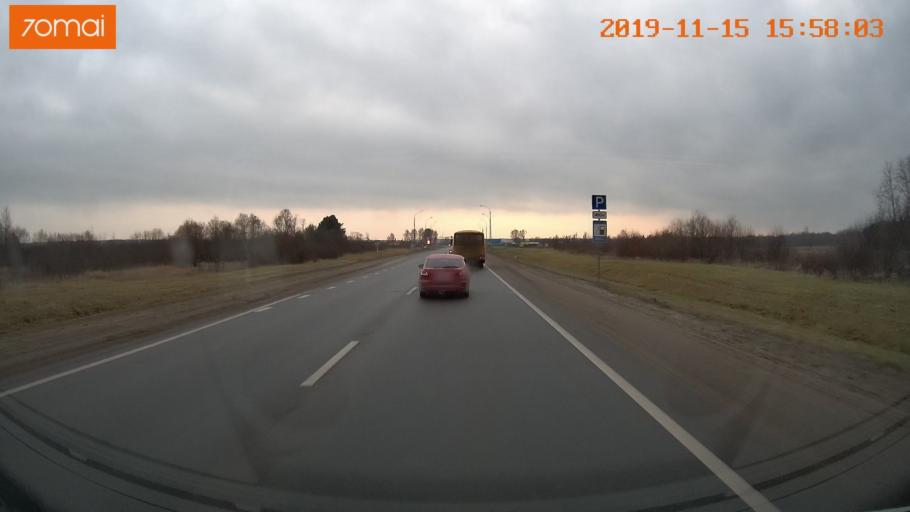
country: RU
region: Jaroslavl
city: Yaroslavl
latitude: 57.8241
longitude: 39.9582
